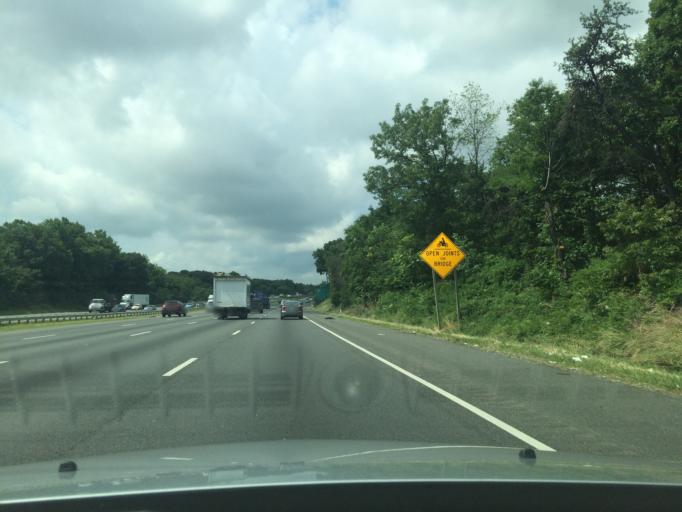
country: US
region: Maryland
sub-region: Prince George's County
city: Forestville
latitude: 38.8339
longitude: -76.8712
